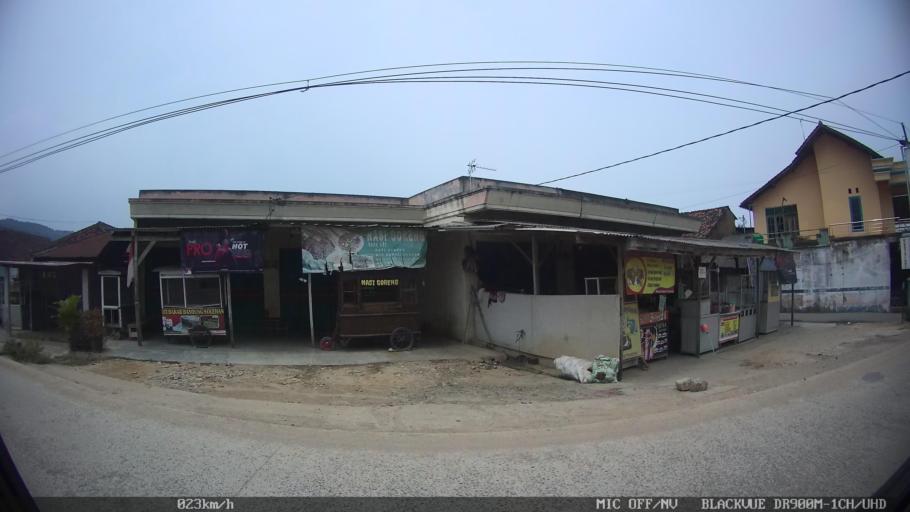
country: ID
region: Lampung
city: Bandarlampung
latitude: -5.4069
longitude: 105.2993
